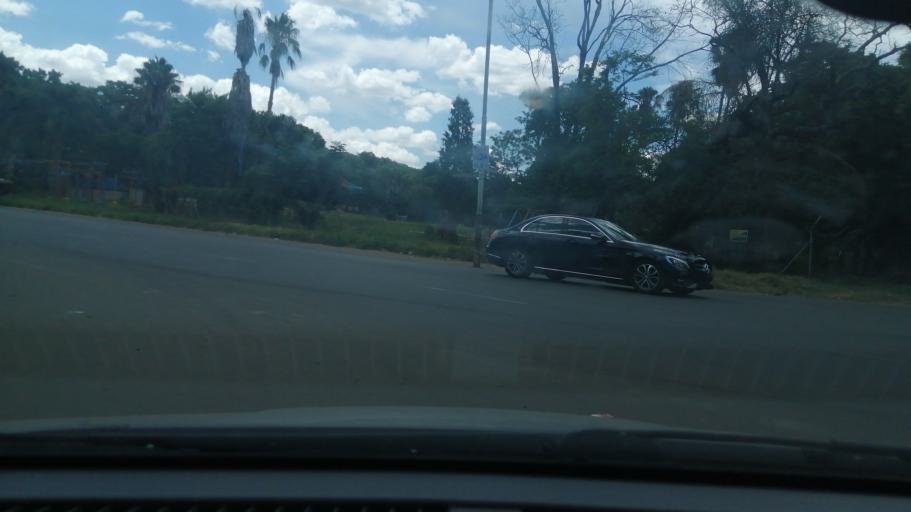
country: ZW
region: Harare
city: Harare
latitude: -17.8193
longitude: 31.0589
